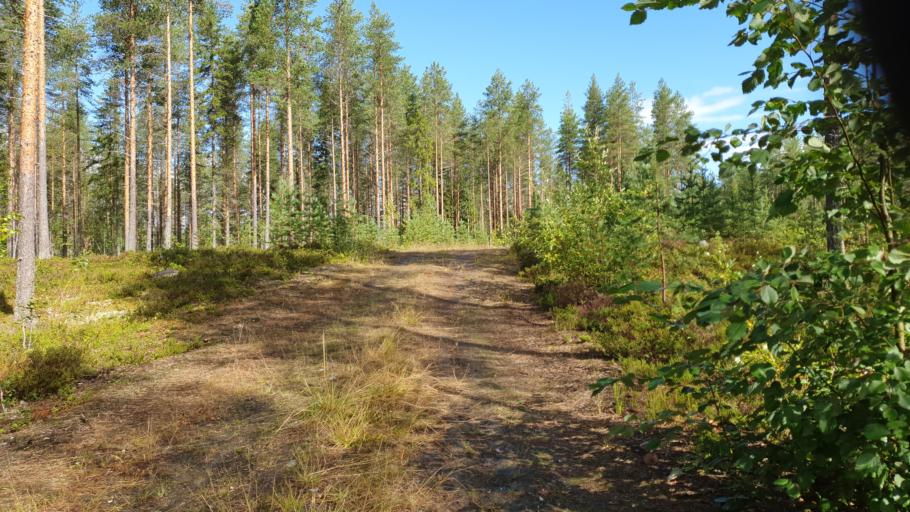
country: FI
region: Kainuu
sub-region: Kehys-Kainuu
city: Kuhmo
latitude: 64.1309
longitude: 29.3798
